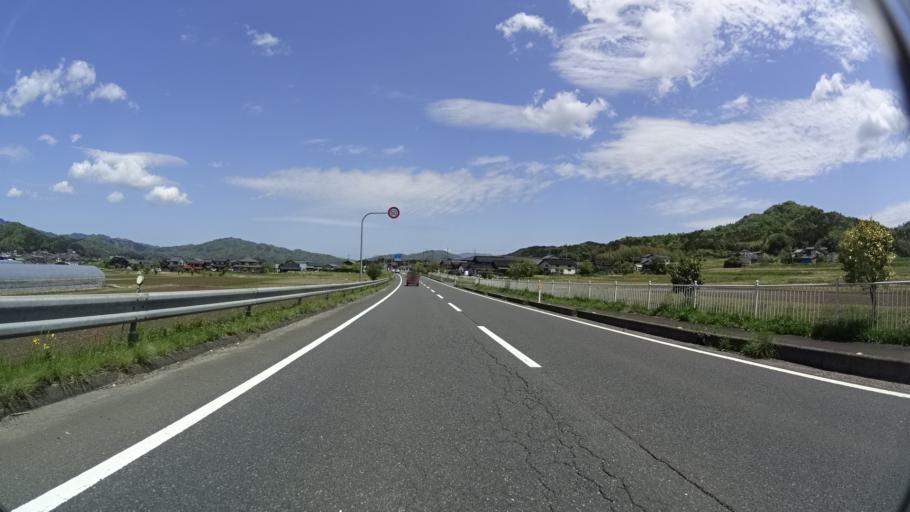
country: JP
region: Kyoto
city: Miyazu
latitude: 35.4986
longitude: 135.1023
